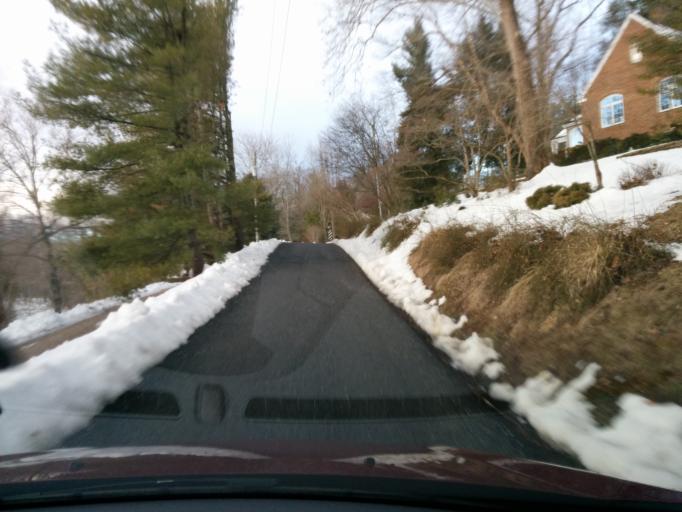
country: US
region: Virginia
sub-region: City of Lexington
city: Lexington
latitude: 37.7829
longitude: -79.4530
